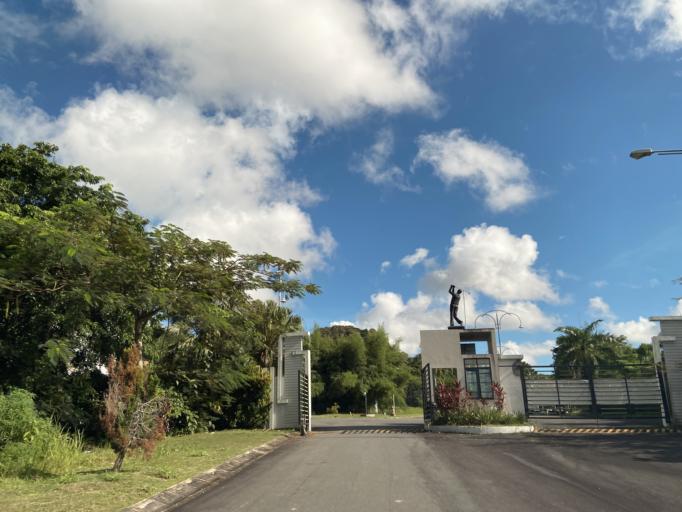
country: SG
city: Singapore
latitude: 1.0953
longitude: 104.0308
